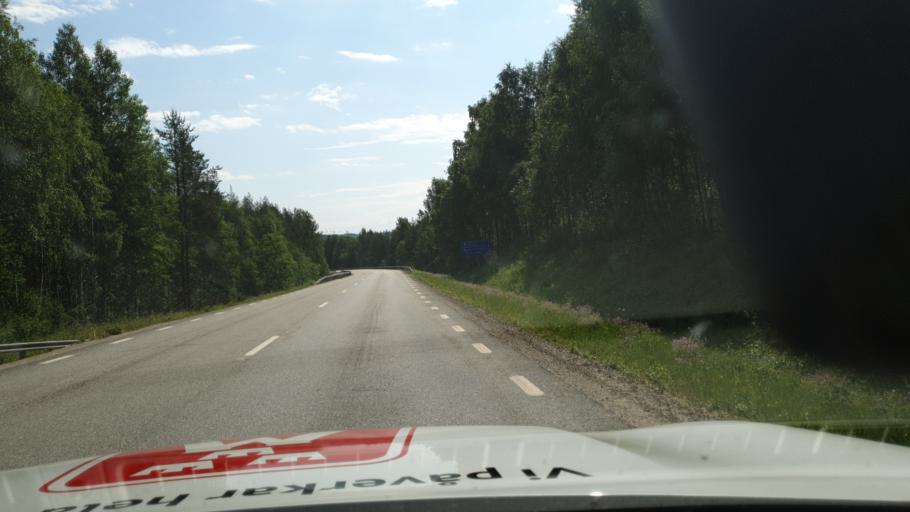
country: SE
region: Vaesterbotten
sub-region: Vindelns Kommun
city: Vindeln
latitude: 64.3149
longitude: 19.5864
